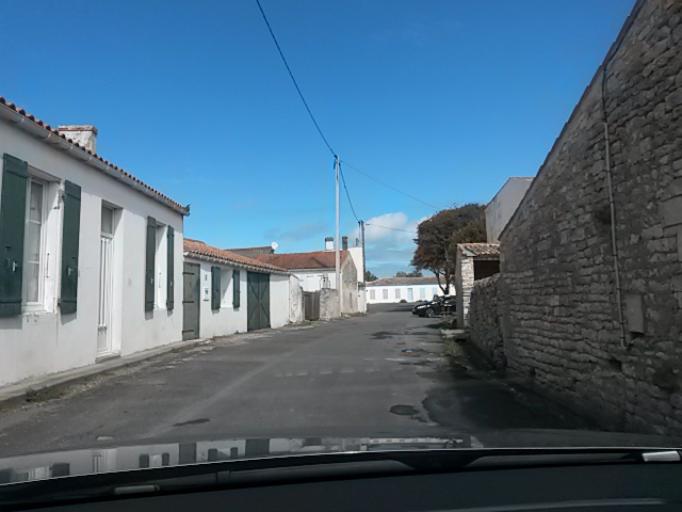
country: FR
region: Poitou-Charentes
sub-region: Departement de la Charente-Maritime
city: Dolus-d'Oleron
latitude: 45.9367
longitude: -1.3565
